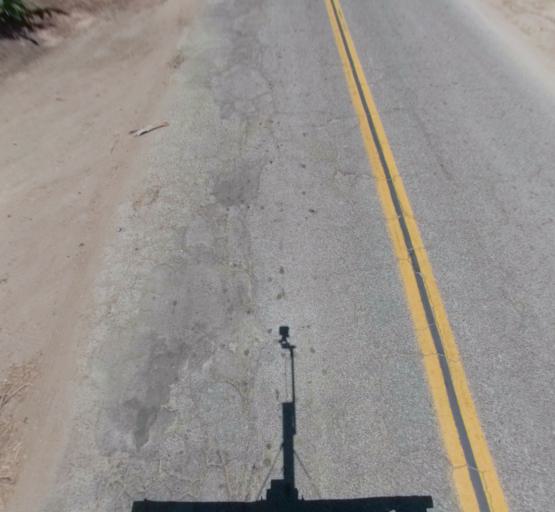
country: US
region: California
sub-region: Madera County
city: Parkwood
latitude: 36.8514
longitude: -120.1103
